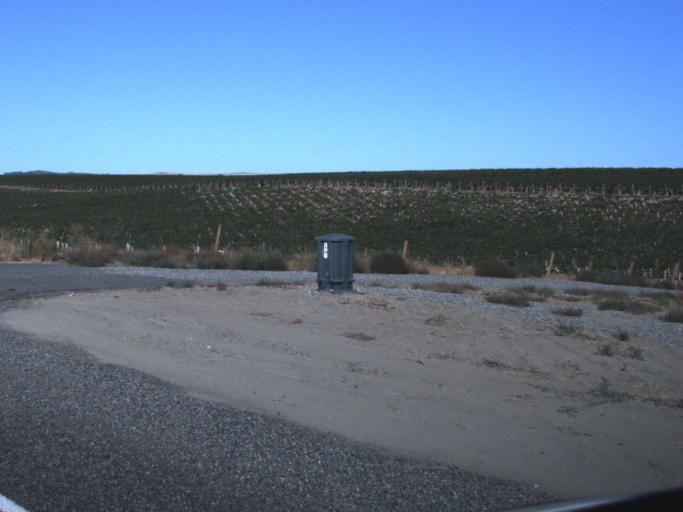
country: US
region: Washington
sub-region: Benton County
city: Benton City
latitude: 46.2624
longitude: -119.4582
